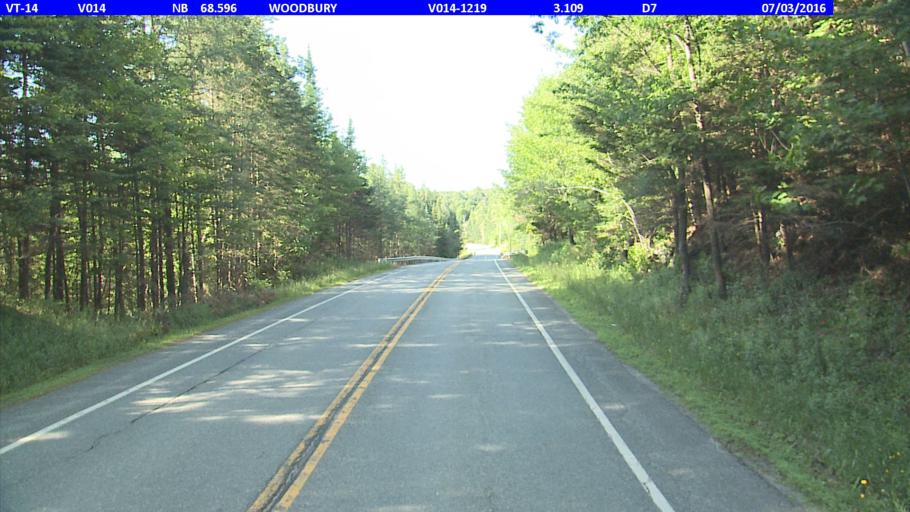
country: US
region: Vermont
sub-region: Caledonia County
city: Hardwick
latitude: 44.4330
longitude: -72.4139
